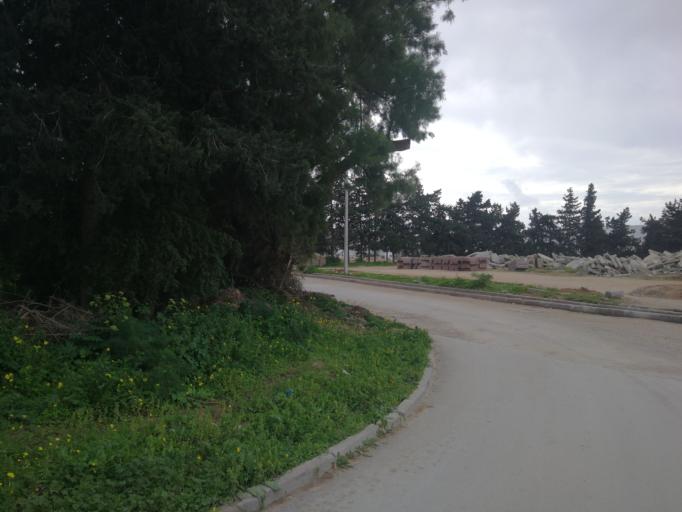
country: TN
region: Tunis
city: Al Marsa
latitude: 36.9089
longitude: 10.3013
